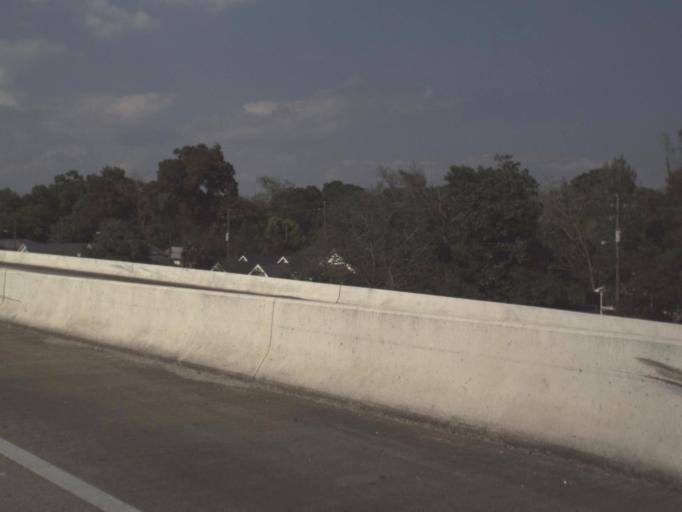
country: US
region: Florida
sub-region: Escambia County
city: Pensacola
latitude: 30.4246
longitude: -87.2145
